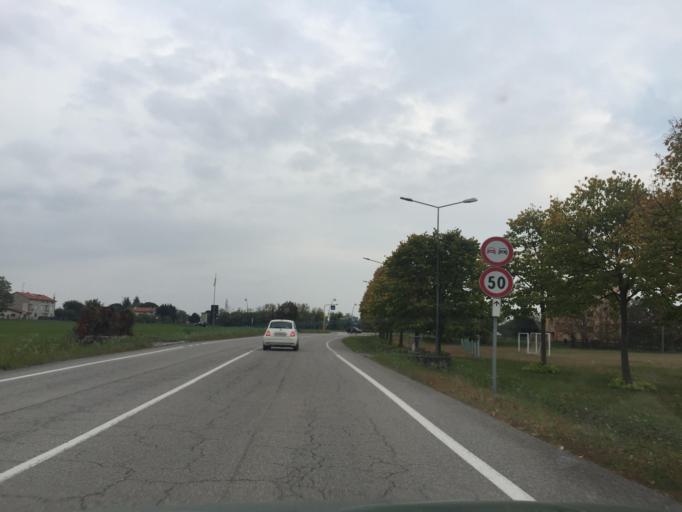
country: IT
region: Friuli Venezia Giulia
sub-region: Provincia di Pordenone
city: Montereale Valcellina
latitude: 46.1531
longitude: 12.6597
